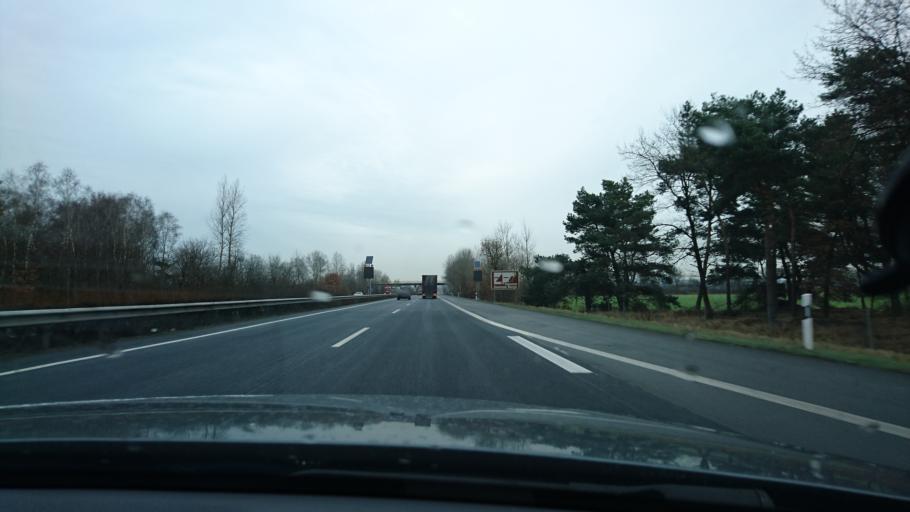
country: DE
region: Lower Saxony
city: Rieste
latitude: 52.4706
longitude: 8.0543
